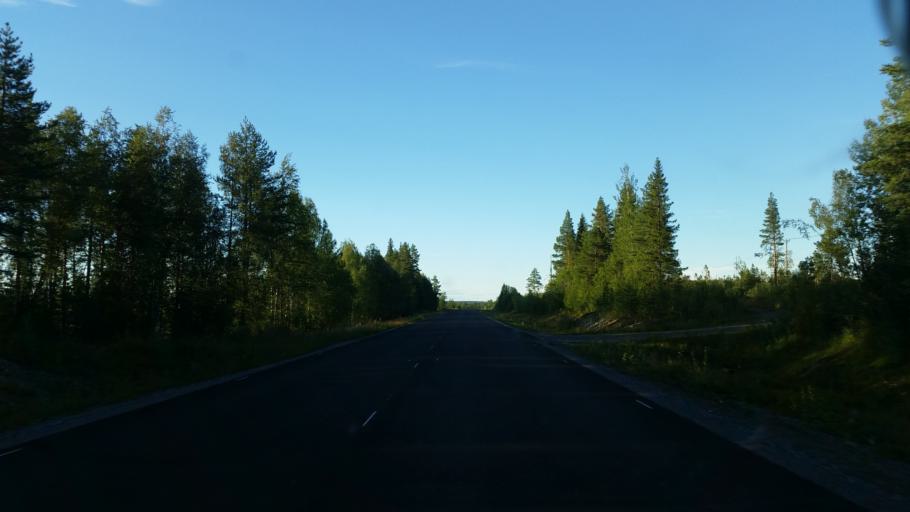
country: SE
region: Vaesterbotten
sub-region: Dorotea Kommun
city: Dorotea
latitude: 64.3135
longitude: 16.6067
